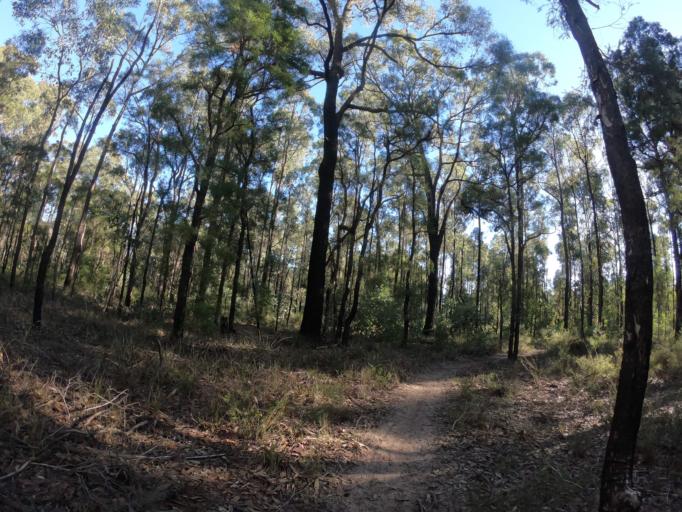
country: AU
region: New South Wales
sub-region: Hawkesbury
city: South Windsor
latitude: -33.6434
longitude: 150.7922
